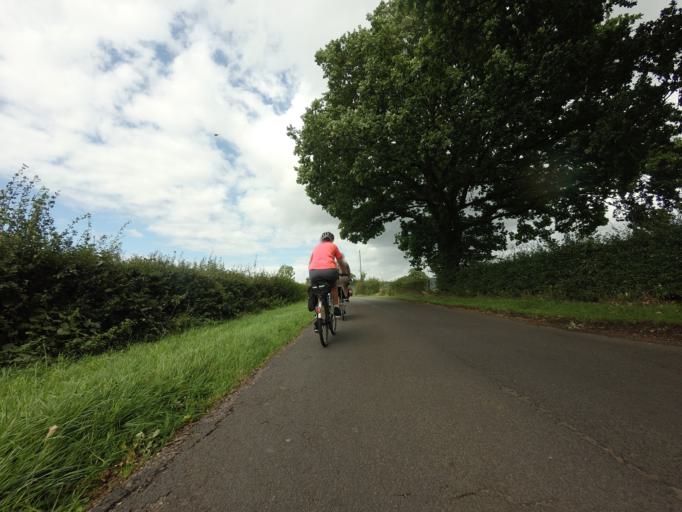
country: GB
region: England
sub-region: Kent
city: Sevenoaks
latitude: 51.2971
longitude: 0.1779
